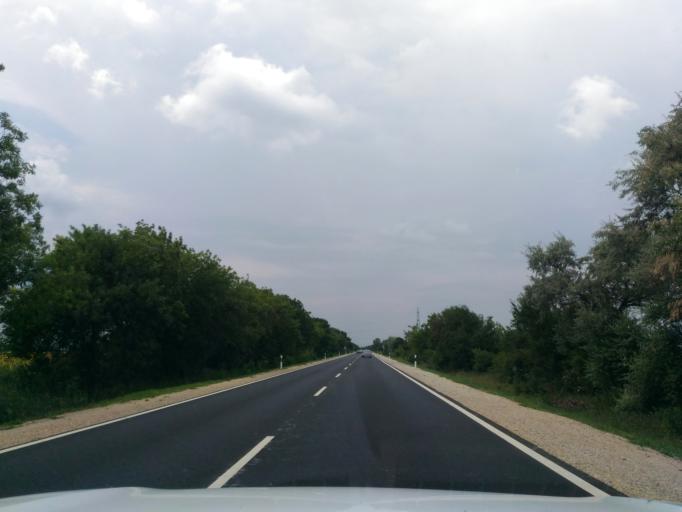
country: HU
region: Jasz-Nagykun-Szolnok
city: Szolnok
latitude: 47.1800
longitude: 20.1289
